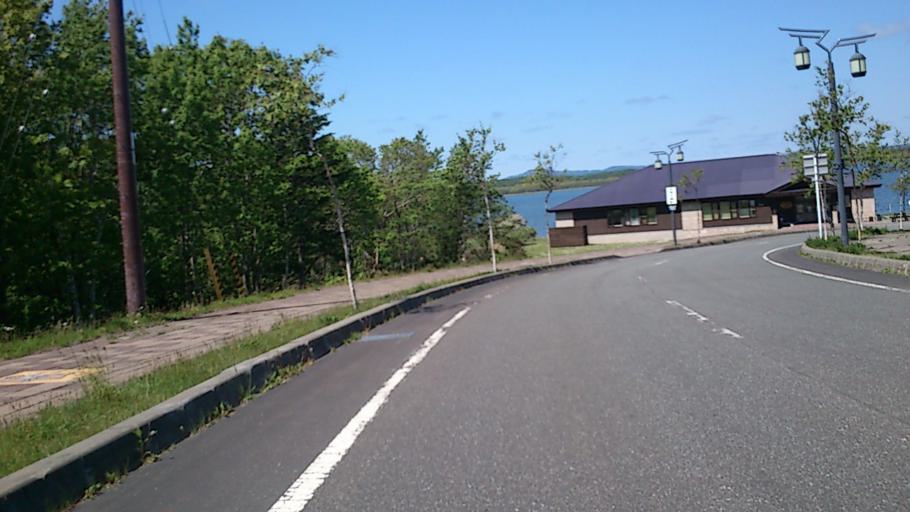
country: JP
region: Hokkaido
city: Makubetsu
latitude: 45.1245
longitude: 142.3477
